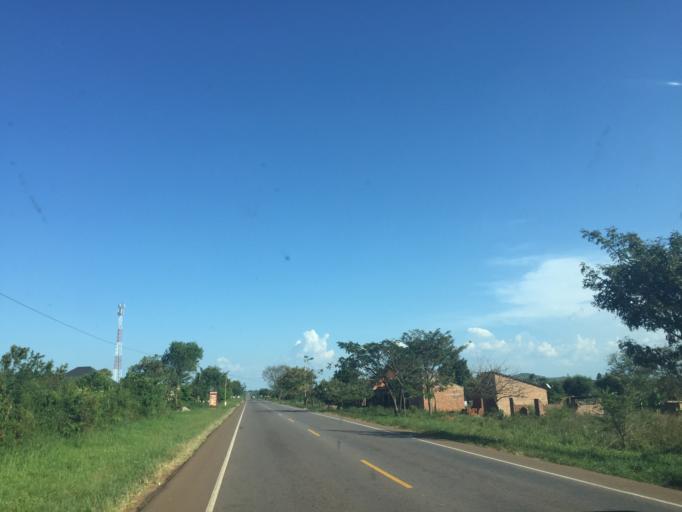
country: UG
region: Central Region
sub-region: Nakasongola District
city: Nakasongola
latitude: 1.3604
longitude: 32.3684
